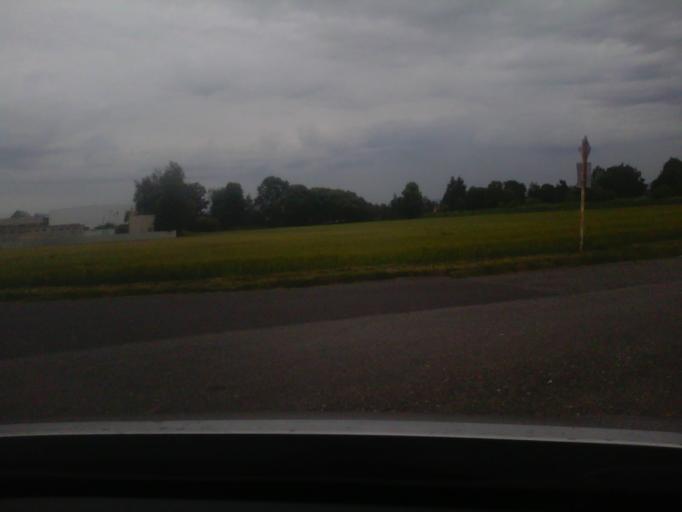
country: CZ
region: Olomoucky
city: Litovel
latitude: 49.7097
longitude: 17.0778
